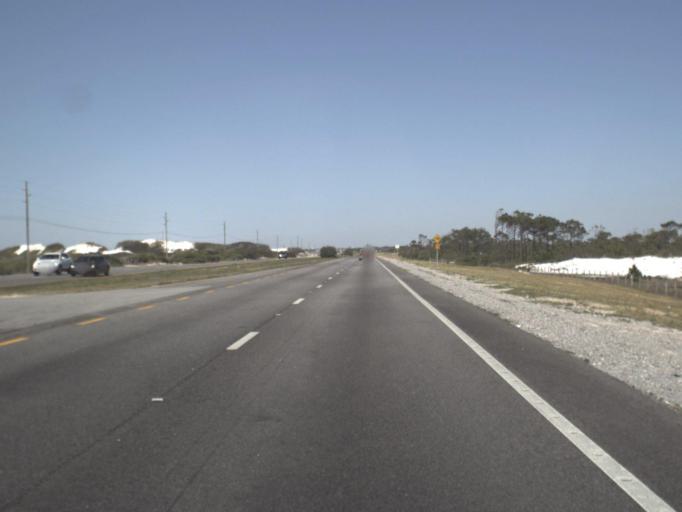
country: US
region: Florida
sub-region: Okaloosa County
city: Destin
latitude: 30.3903
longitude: -86.5389
